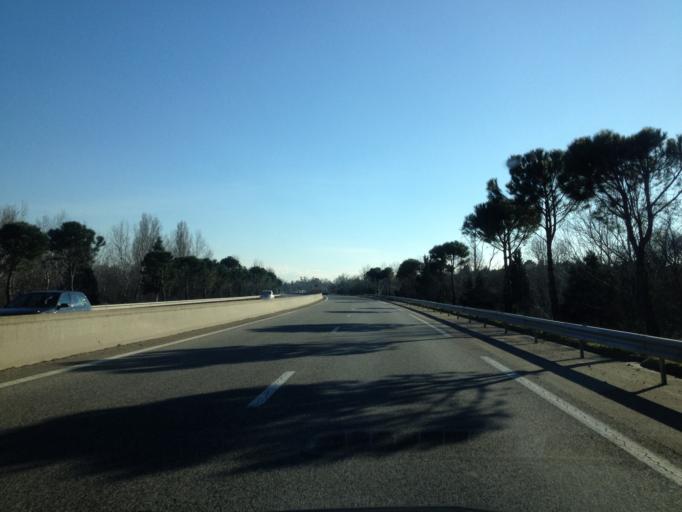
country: FR
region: Provence-Alpes-Cote d'Azur
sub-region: Departement du Vaucluse
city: Sorgues
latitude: 44.0047
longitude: 4.8633
